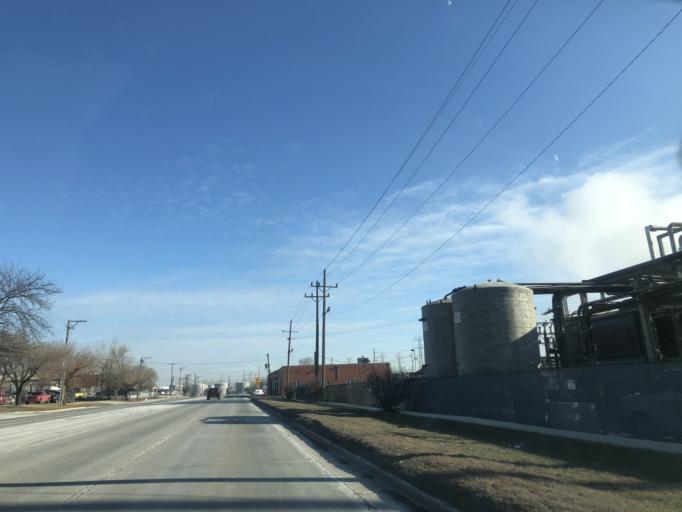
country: US
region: Illinois
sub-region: Cook County
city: Cicero
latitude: 41.8218
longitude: -87.7500
